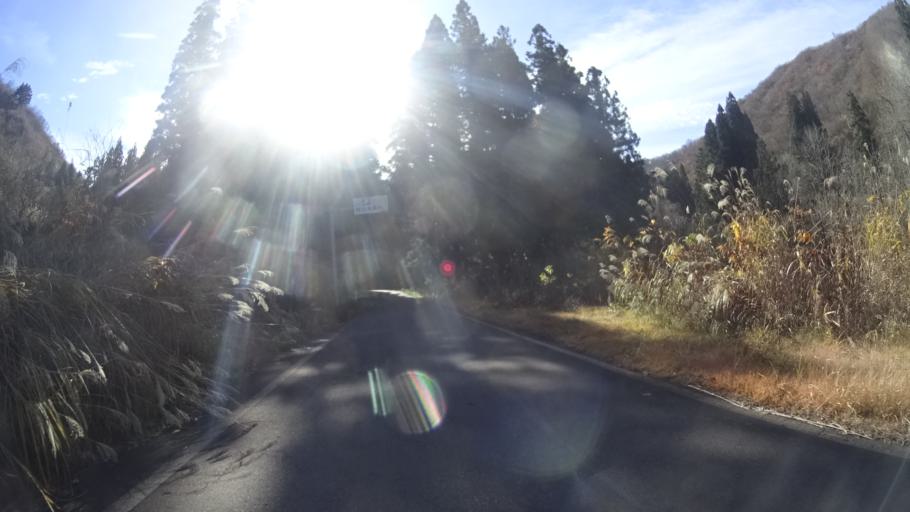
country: JP
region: Niigata
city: Muikamachi
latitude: 37.1751
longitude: 139.0864
